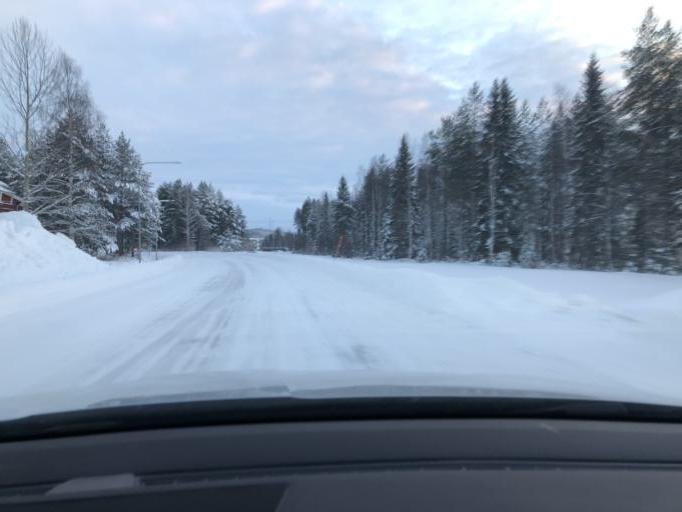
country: SE
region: Norrbotten
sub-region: Lulea Kommun
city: Bergnaset
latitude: 65.6192
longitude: 22.1180
